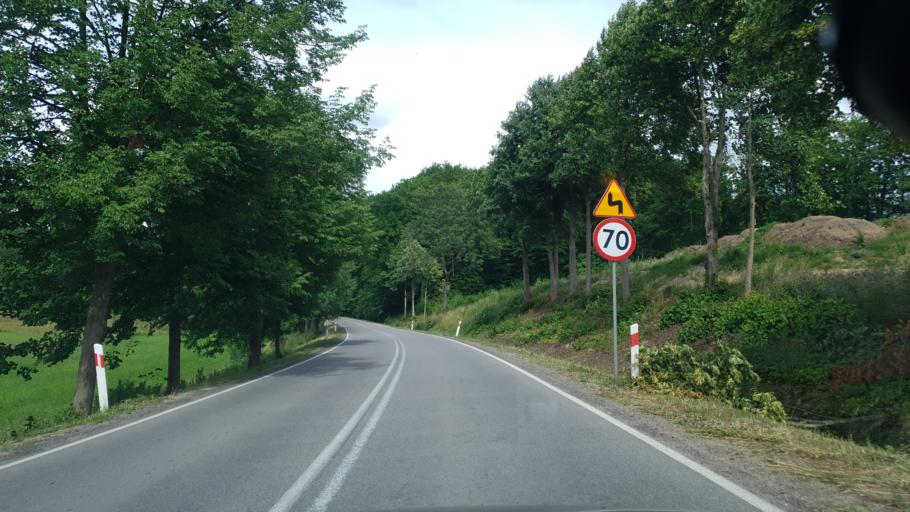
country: PL
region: Pomeranian Voivodeship
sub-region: Powiat kartuski
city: Kartuzy
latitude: 54.3136
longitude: 18.1612
